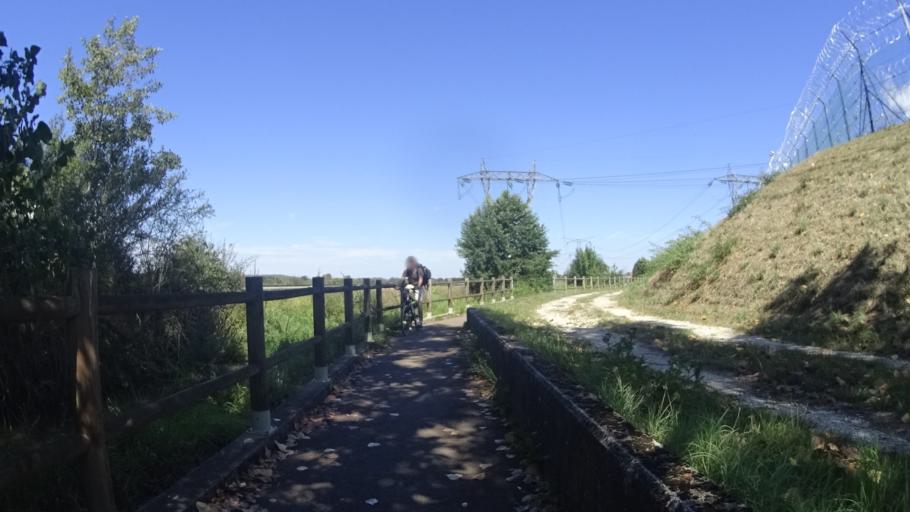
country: FR
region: Centre
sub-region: Departement du Cher
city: Belleville-sur-Loire
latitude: 47.5063
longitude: 2.8680
